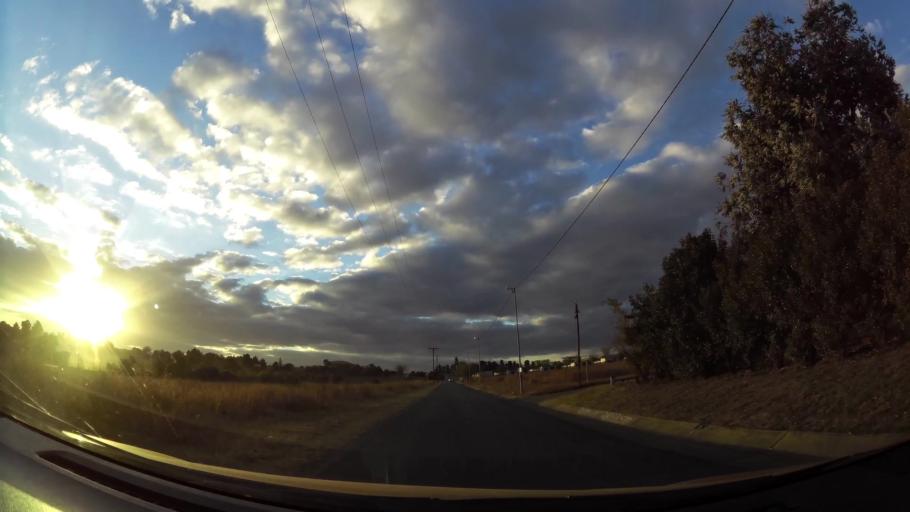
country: ZA
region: Gauteng
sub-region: City of Johannesburg Metropolitan Municipality
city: Midrand
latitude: -25.9994
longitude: 28.1509
